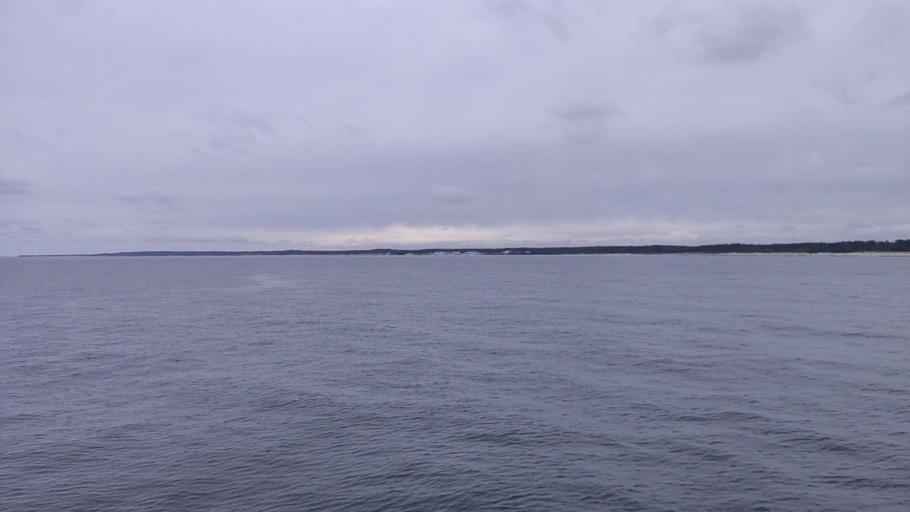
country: PL
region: Pomeranian Voivodeship
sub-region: Powiat slupski
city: Ustka
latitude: 54.5959
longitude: 16.8505
